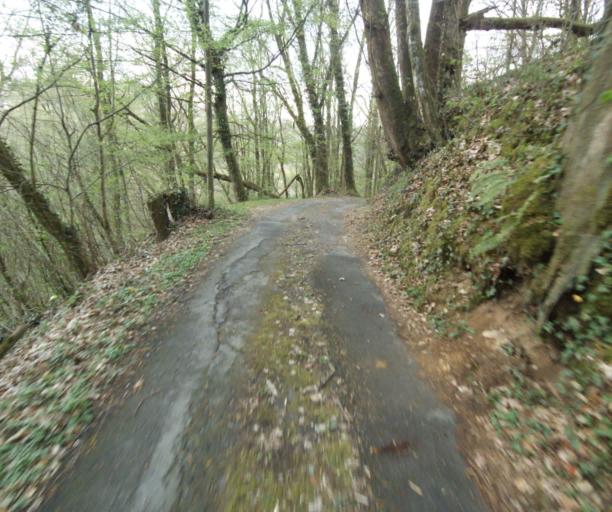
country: FR
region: Limousin
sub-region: Departement de la Correze
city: Tulle
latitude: 45.2511
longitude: 1.7486
